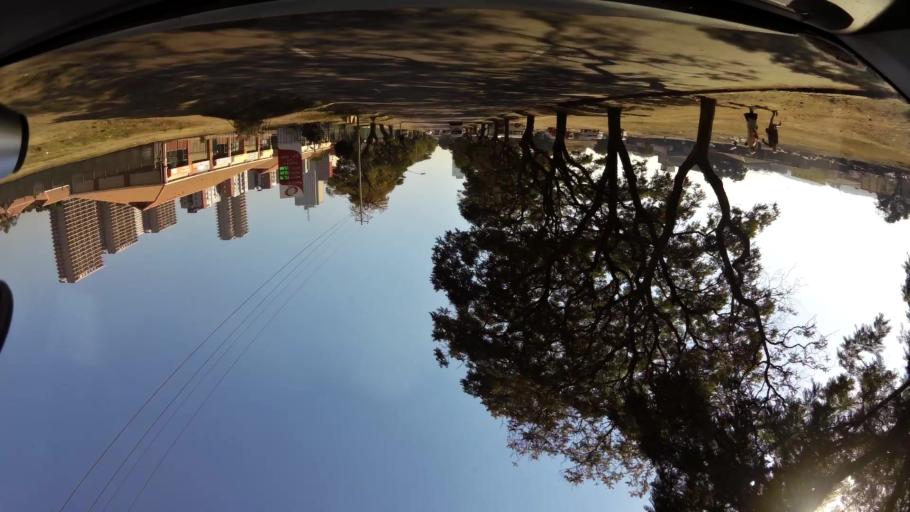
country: ZA
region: Gauteng
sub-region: City of Tshwane Metropolitan Municipality
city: Pretoria
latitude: -25.7427
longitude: 28.1785
